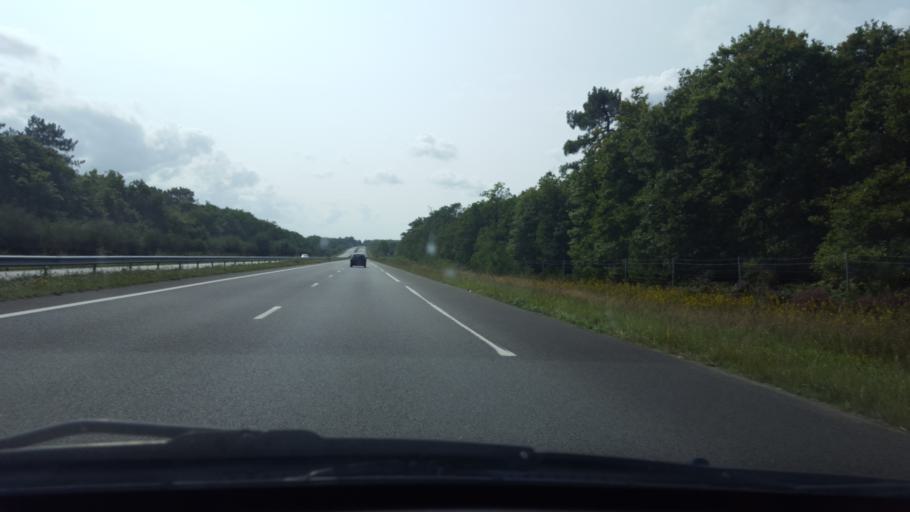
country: FR
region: Pays de la Loire
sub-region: Departement de la Loire-Atlantique
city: Saint-Lumine-de-Coutais
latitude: 47.0092
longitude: -1.7120
